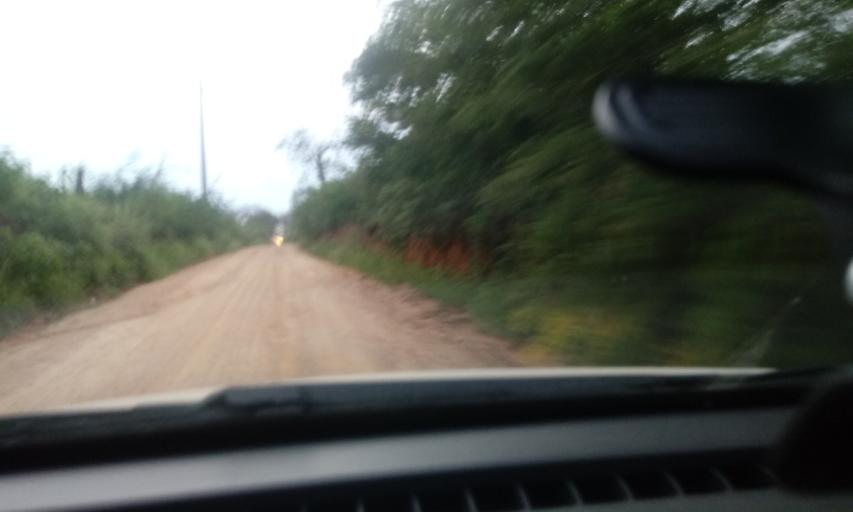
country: BR
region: Bahia
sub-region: Riacho De Santana
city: Riacho de Santana
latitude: -13.8004
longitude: -42.7466
